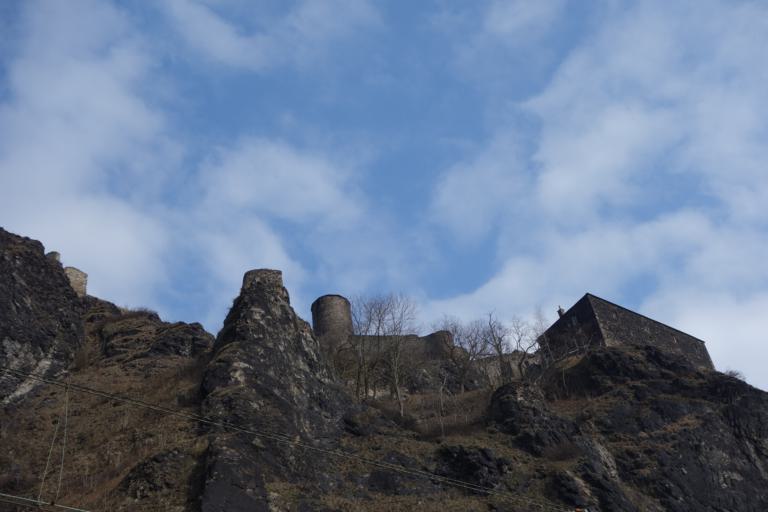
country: CZ
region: Ustecky
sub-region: Okres Usti nad Labem
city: Usti nad Labem
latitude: 50.6398
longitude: 14.0491
